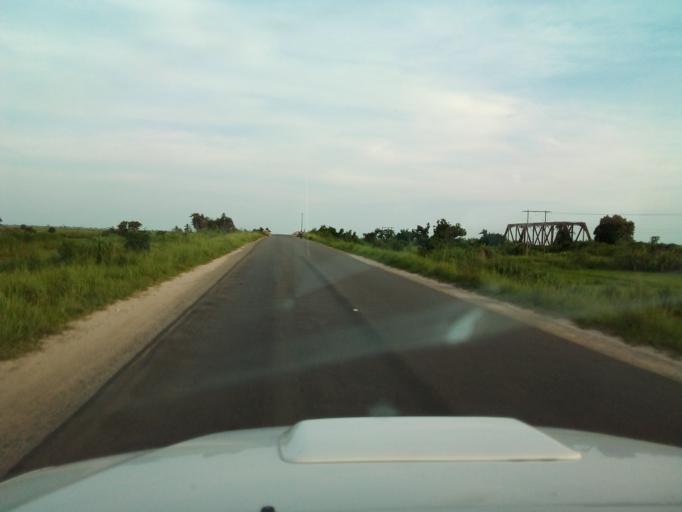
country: MZ
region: Zambezia
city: Quelimane
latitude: -17.6634
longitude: 36.8638
